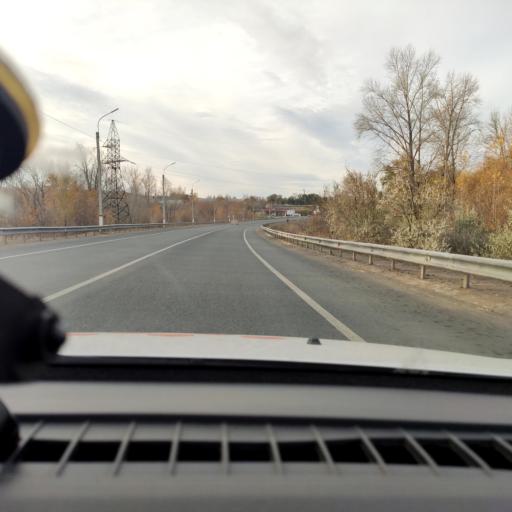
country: RU
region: Samara
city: Novokuybyshevsk
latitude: 53.1237
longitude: 49.9450
